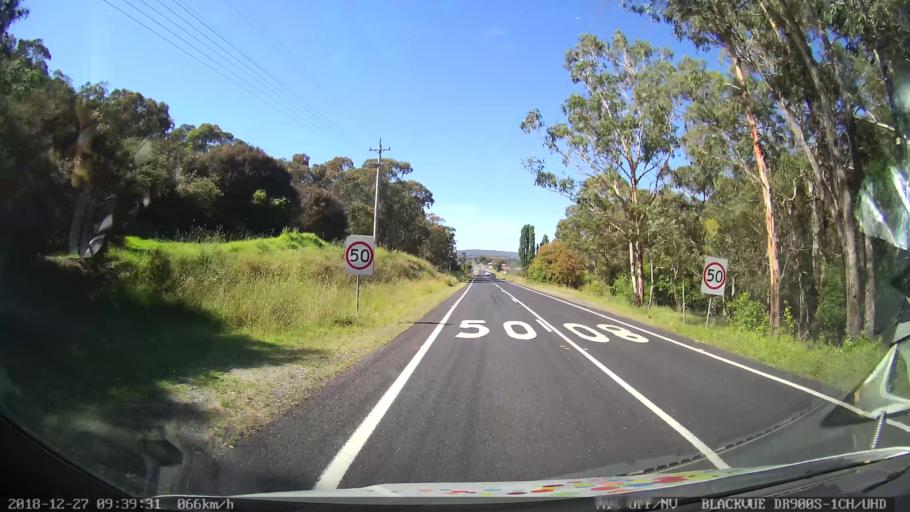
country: AU
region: New South Wales
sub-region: Lithgow
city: Portland
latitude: -33.2935
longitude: 150.0348
